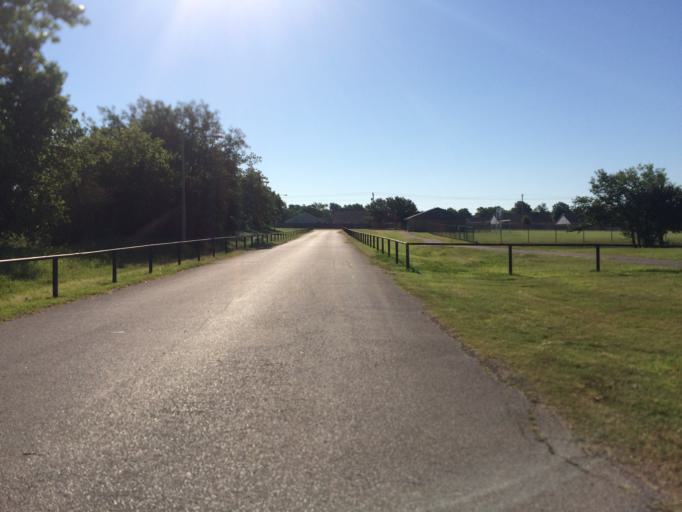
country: US
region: Oklahoma
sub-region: Cleveland County
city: Hall Park
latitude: 35.2384
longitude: -97.4255
